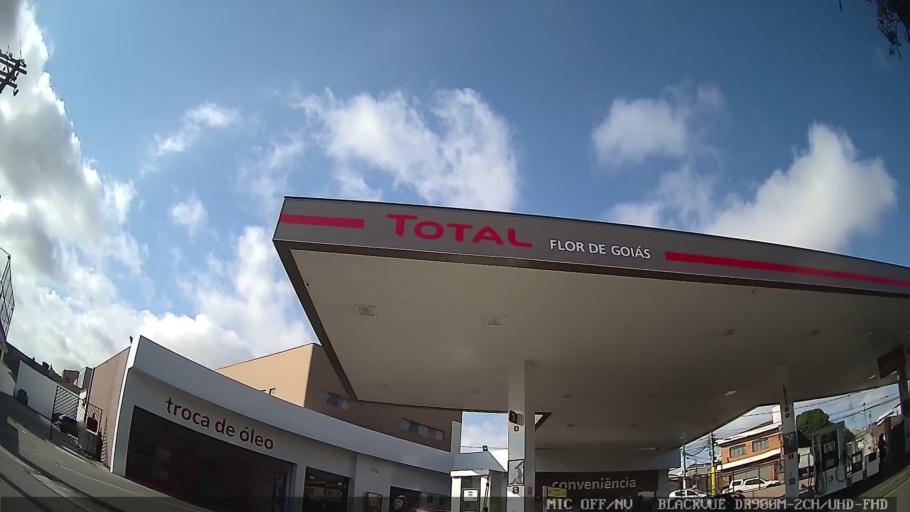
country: BR
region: Sao Paulo
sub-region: Guarulhos
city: Guarulhos
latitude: -23.5432
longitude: -46.4941
